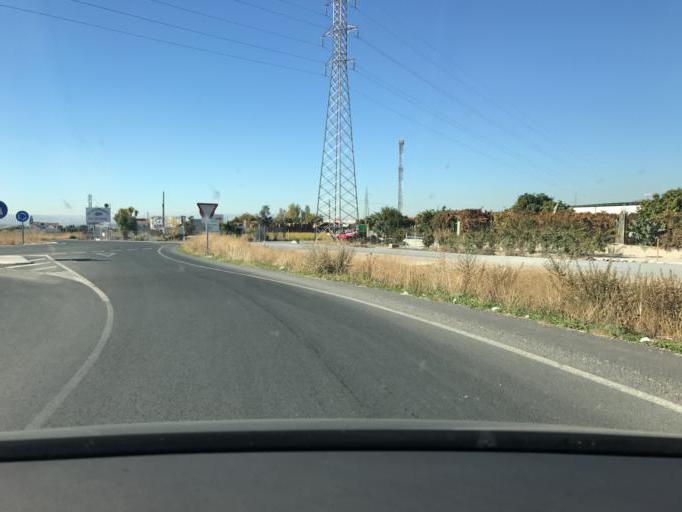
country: ES
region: Andalusia
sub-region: Provincia de Granada
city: Albolote
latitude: 37.2268
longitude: -3.6693
